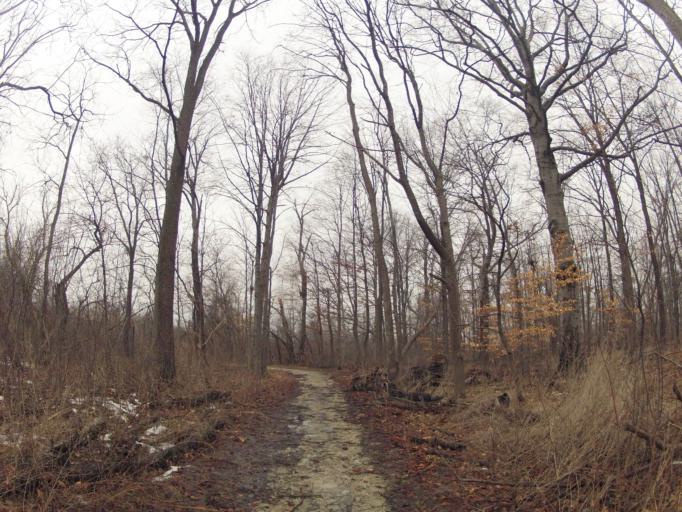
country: CA
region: Ontario
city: Brampton
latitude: 43.6762
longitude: -79.6827
